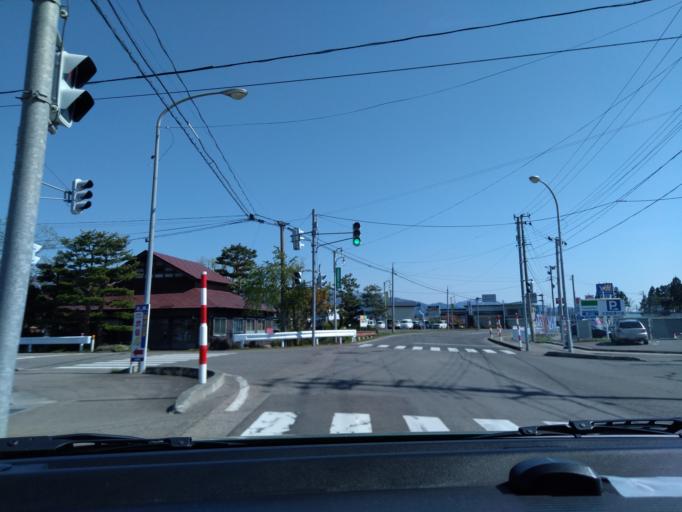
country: JP
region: Akita
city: Kakunodatemachi
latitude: 39.5077
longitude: 140.5958
